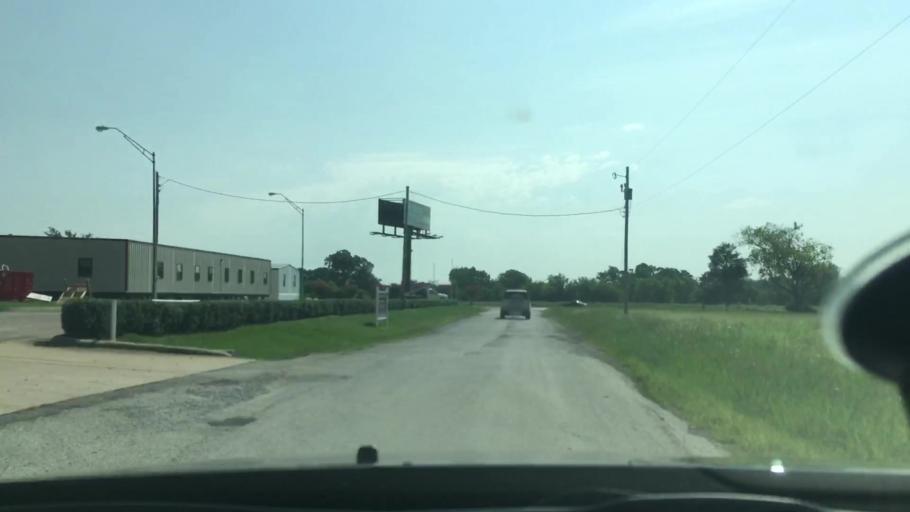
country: US
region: Oklahoma
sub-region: Bryan County
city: Durant
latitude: 34.0556
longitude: -96.3568
